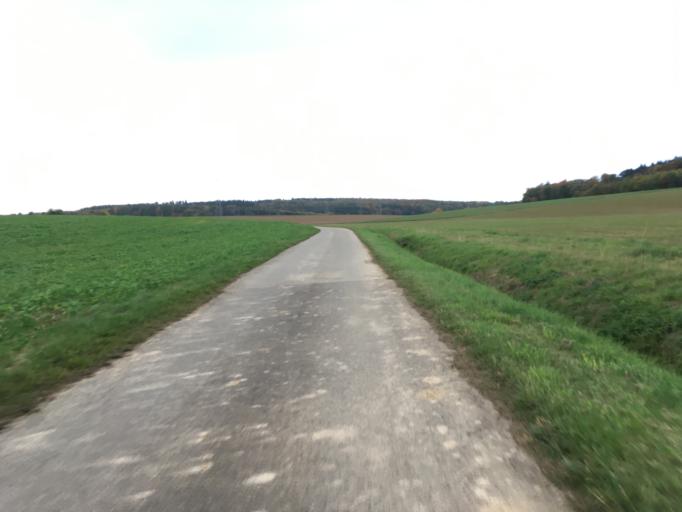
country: DE
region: Baden-Wuerttemberg
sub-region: Karlsruhe Region
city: Osterburken
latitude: 49.4660
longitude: 9.3840
